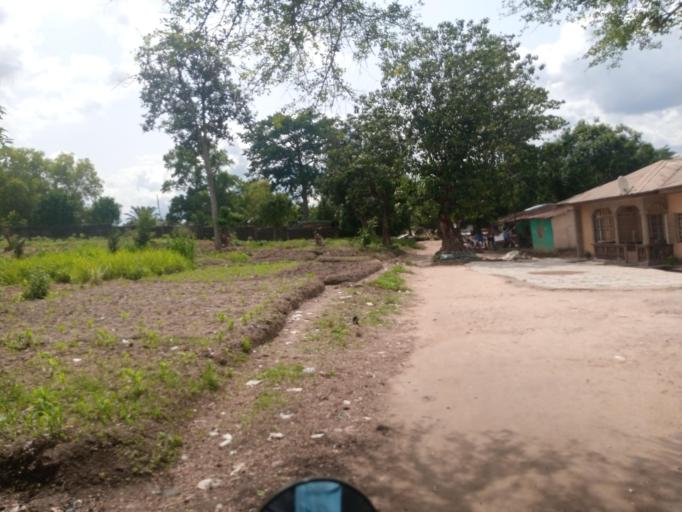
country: SL
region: Southern Province
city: Bo
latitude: 7.9778
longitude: -11.7359
